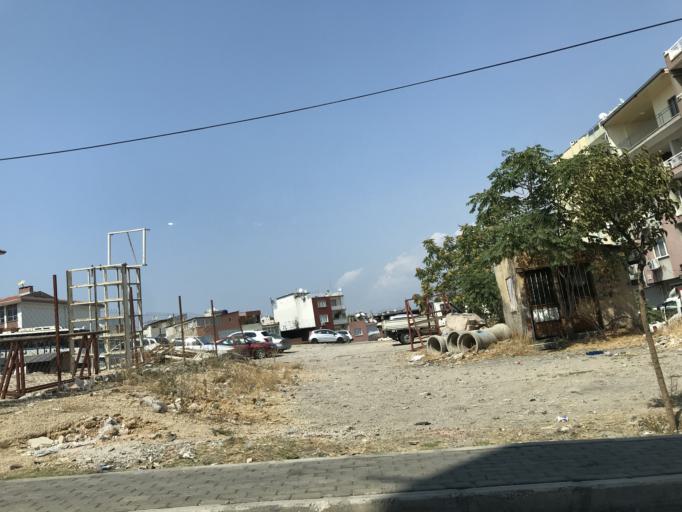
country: TR
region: Izmir
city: Karabaglar
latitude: 38.3892
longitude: 27.1280
